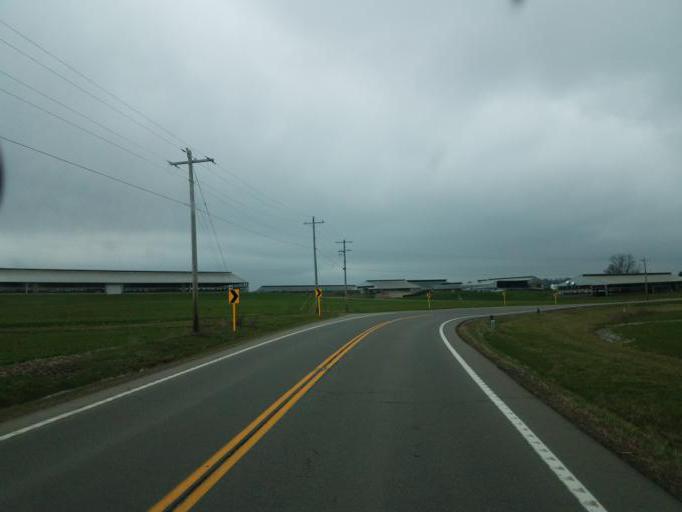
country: US
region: Ohio
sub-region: Ashland County
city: Loudonville
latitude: 40.7496
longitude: -82.2593
